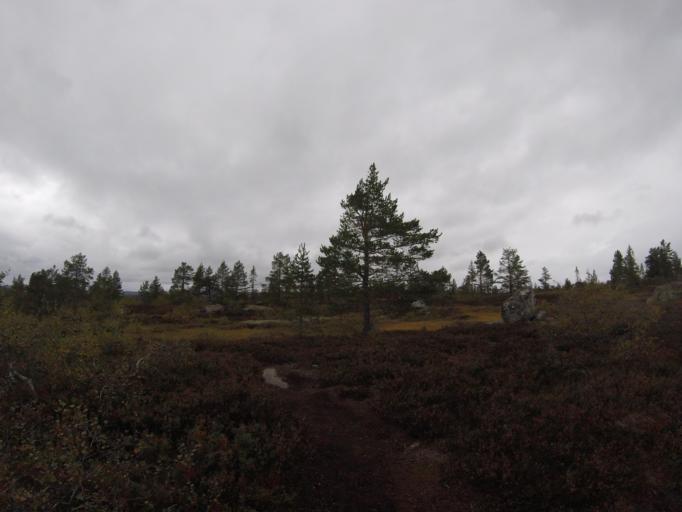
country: NO
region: Buskerud
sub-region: Flesberg
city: Lampeland
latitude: 59.7589
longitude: 9.4006
